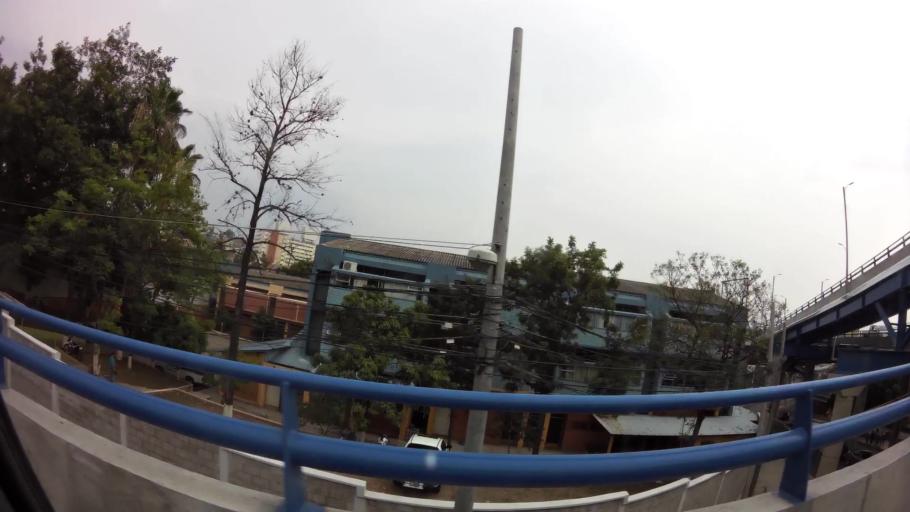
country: HN
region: Francisco Morazan
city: Tegucigalpa
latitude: 14.0879
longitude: -87.2022
